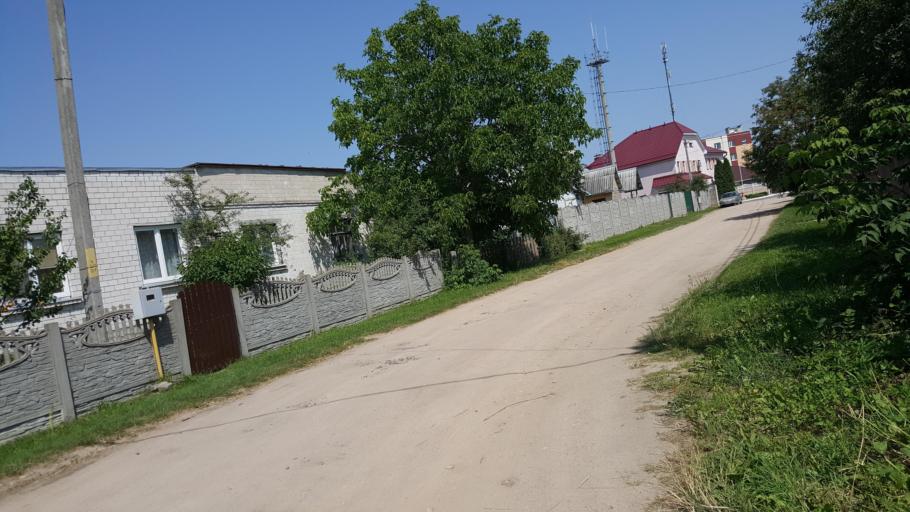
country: BY
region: Brest
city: Zhabinka
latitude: 52.1953
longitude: 24.0068
